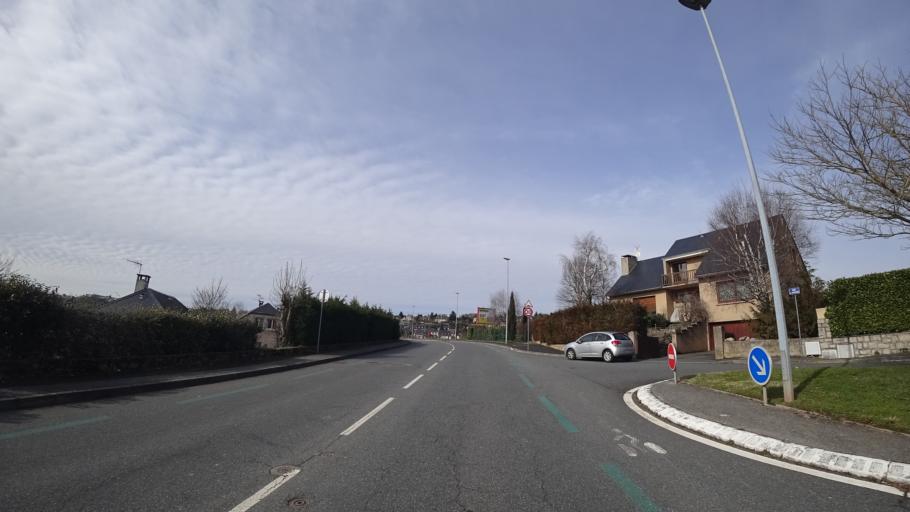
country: FR
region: Midi-Pyrenees
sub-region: Departement de l'Aveyron
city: Rodez
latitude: 44.3670
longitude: 2.5613
